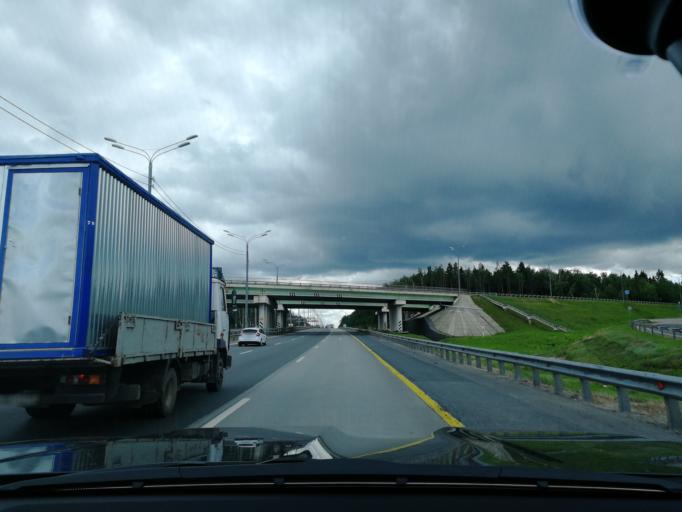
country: RU
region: Moskovskaya
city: Barybino
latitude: 55.2371
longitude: 37.8691
